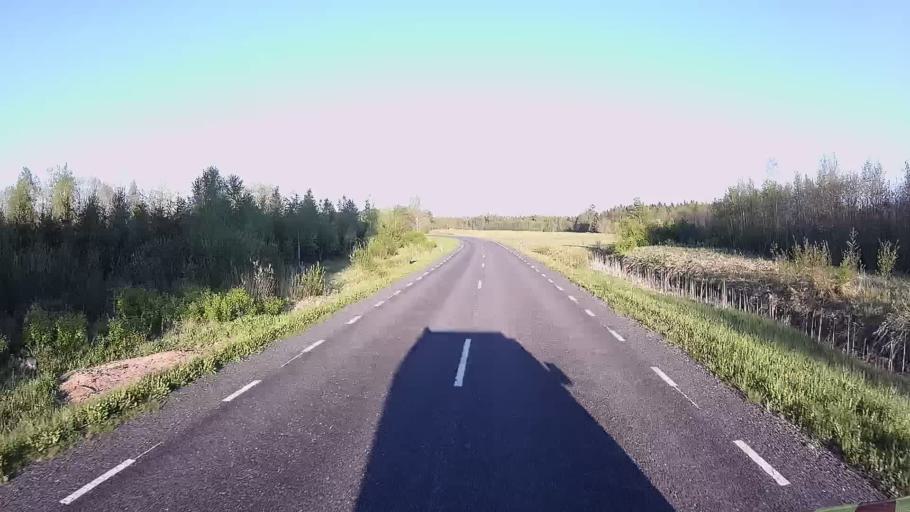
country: EE
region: Jogevamaa
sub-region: Poltsamaa linn
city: Poltsamaa
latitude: 58.5225
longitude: 25.9686
